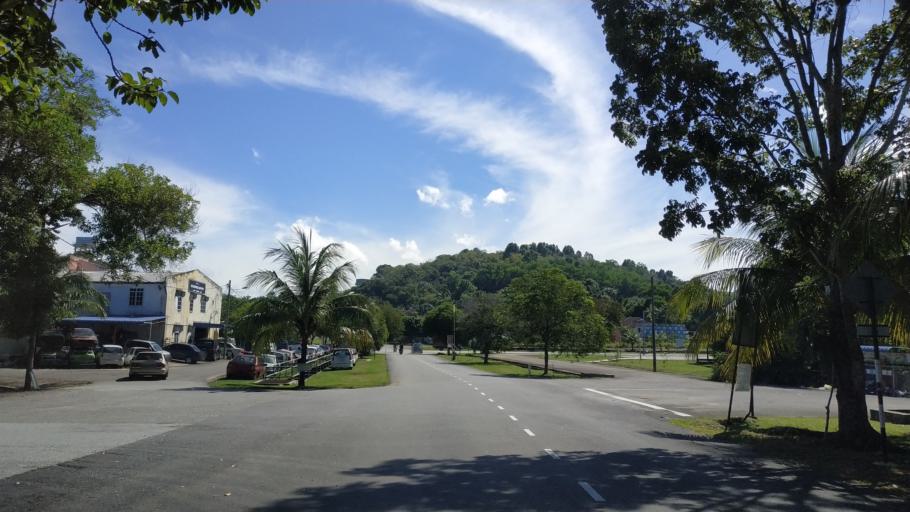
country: MY
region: Kedah
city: Kulim
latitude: 5.3379
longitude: 100.5367
